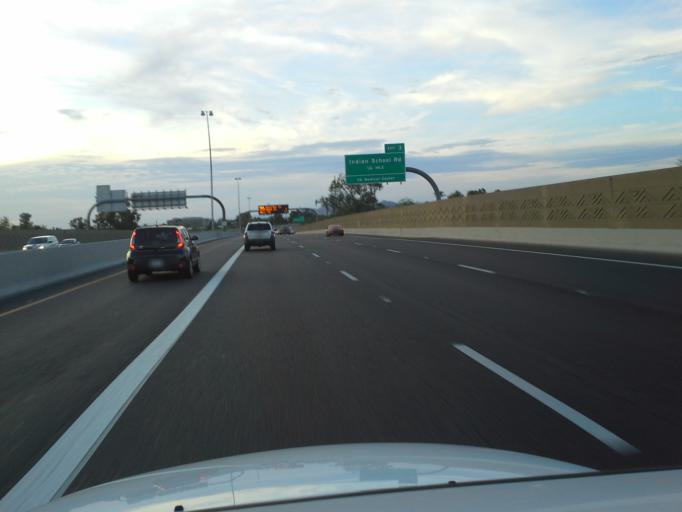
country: US
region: Arizona
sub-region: Maricopa County
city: Phoenix
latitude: 33.4872
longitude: -112.0418
